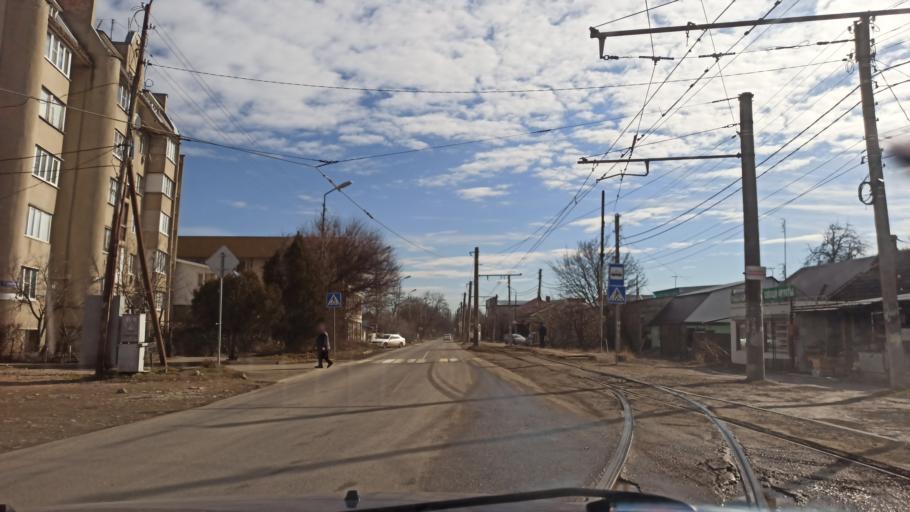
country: RU
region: Stavropol'skiy
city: Vinsady
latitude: 44.0499
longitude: 42.9817
